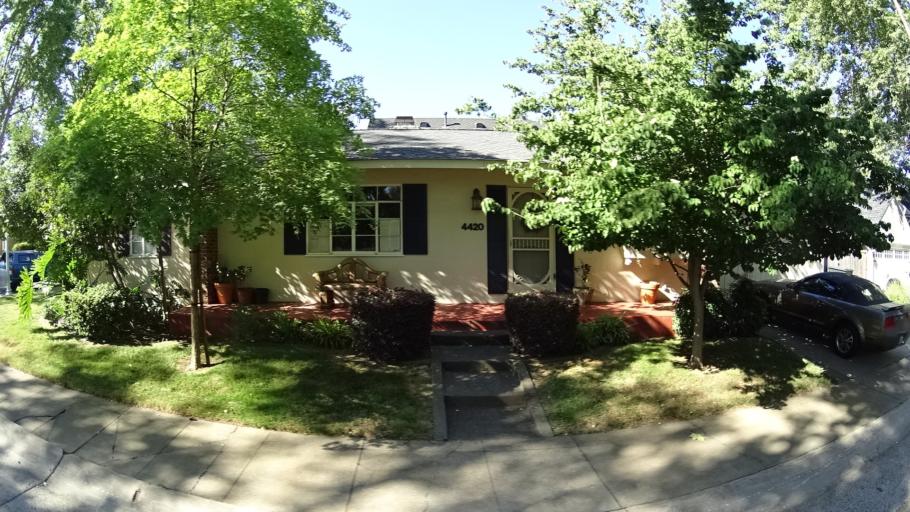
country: US
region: California
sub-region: Sacramento County
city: Sacramento
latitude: 38.5699
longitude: -121.4473
